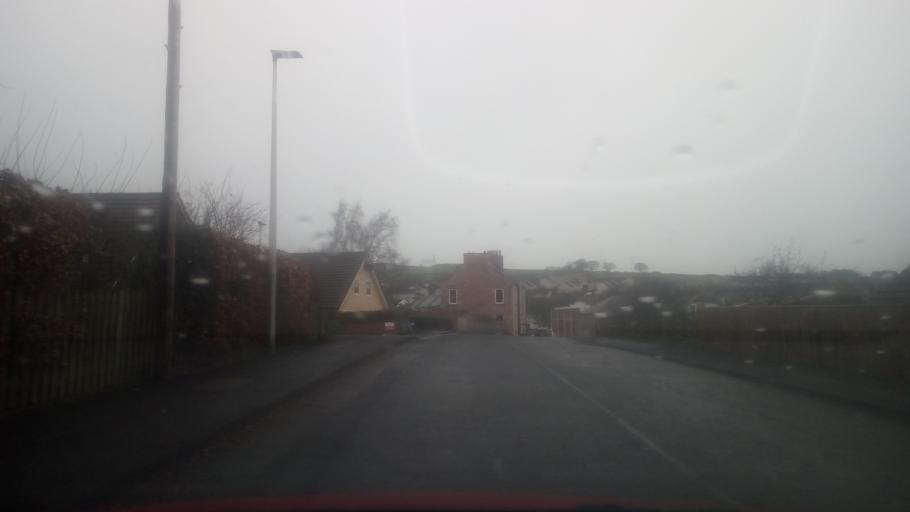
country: GB
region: Scotland
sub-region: The Scottish Borders
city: Earlston
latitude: 55.6365
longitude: -2.6760
